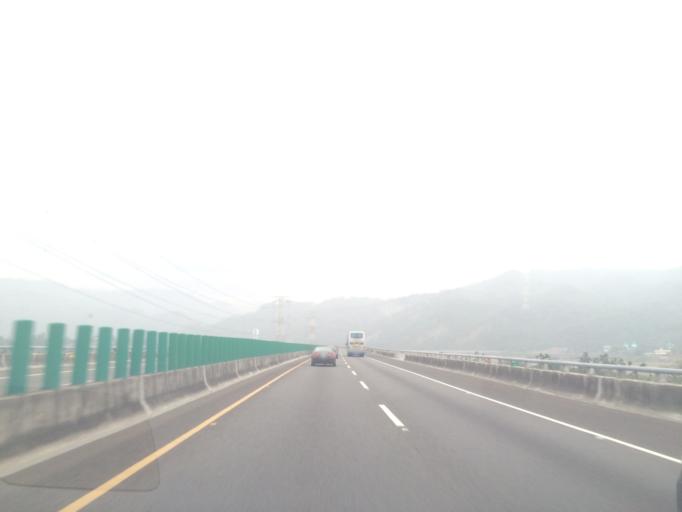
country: TW
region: Taiwan
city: Zhongxing New Village
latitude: 23.9912
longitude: 120.7533
